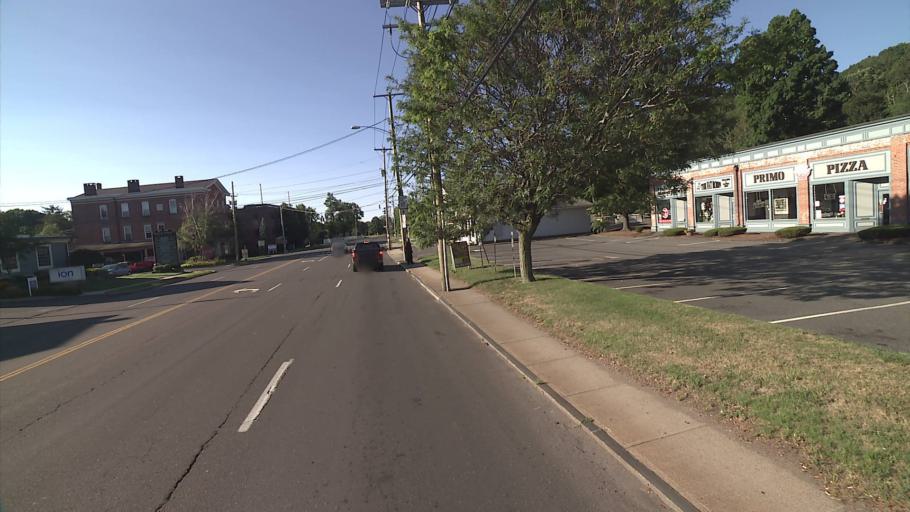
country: US
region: Connecticut
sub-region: New Haven County
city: Hamden
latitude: 41.4045
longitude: -72.8986
